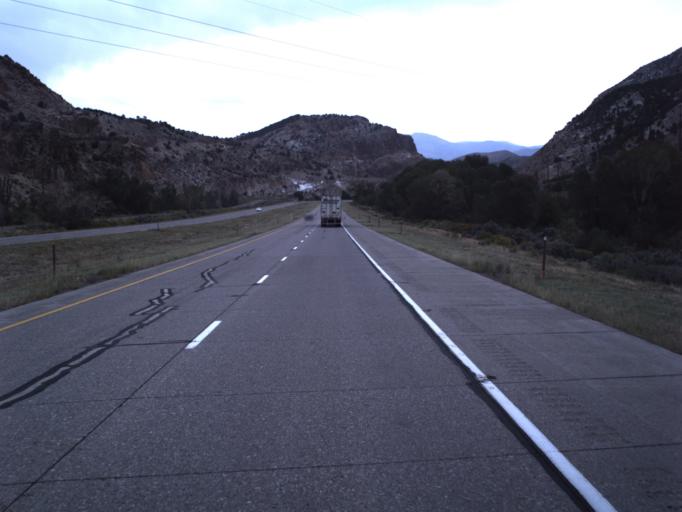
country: US
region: Utah
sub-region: Sevier County
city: Monroe
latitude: 38.5785
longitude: -112.3129
